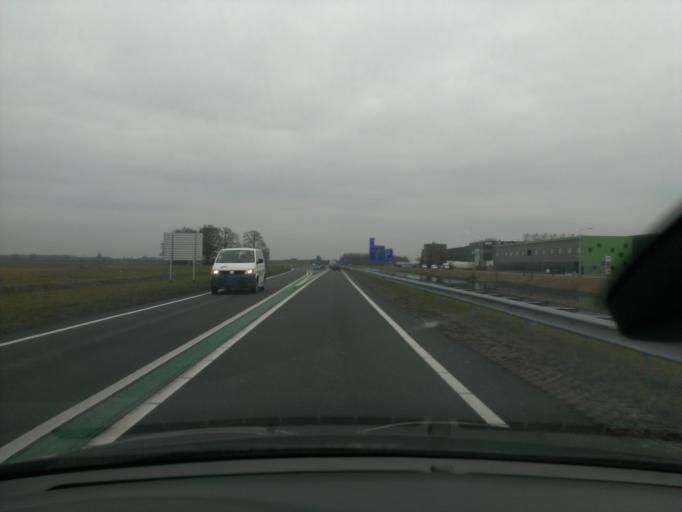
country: NL
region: Overijssel
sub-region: Gemeente Twenterand
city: Vriezenveen
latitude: 52.4100
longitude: 6.6366
